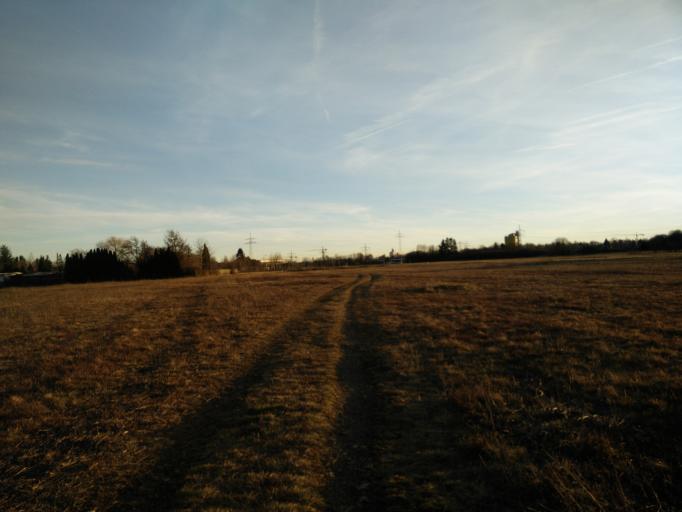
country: DE
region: Bavaria
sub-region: Upper Bavaria
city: Pasing
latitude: 48.1692
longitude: 11.4306
